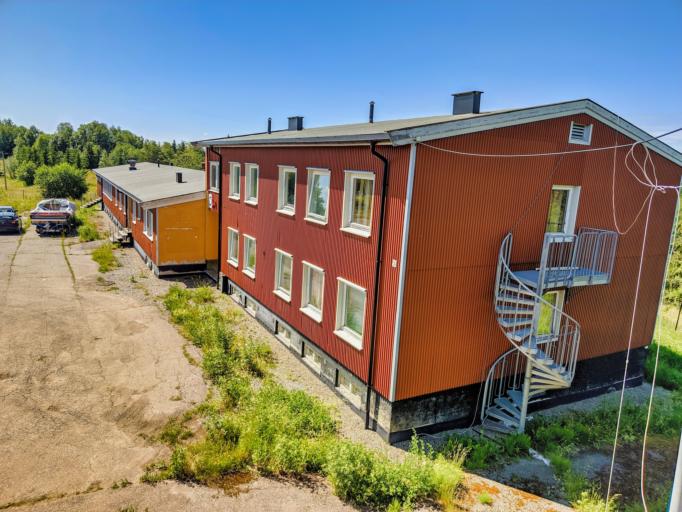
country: NO
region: Akershus
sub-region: Nes
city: Neskollen
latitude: 60.1333
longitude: 11.2849
